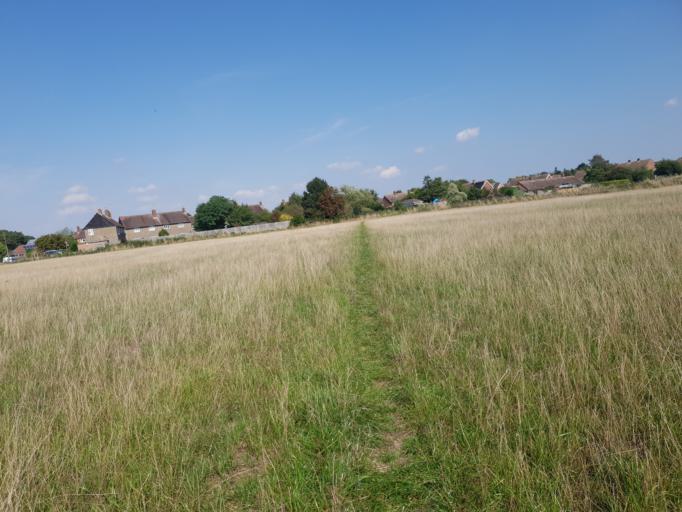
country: GB
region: England
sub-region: Suffolk
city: East Bergholt
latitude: 51.9235
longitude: 0.9800
